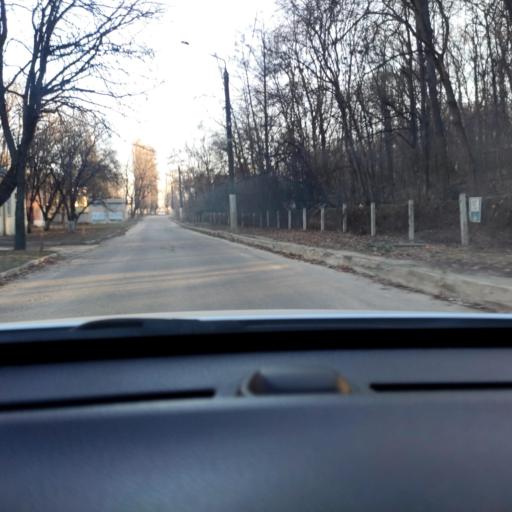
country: RU
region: Voronezj
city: Voronezh
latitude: 51.7266
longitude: 39.2302
